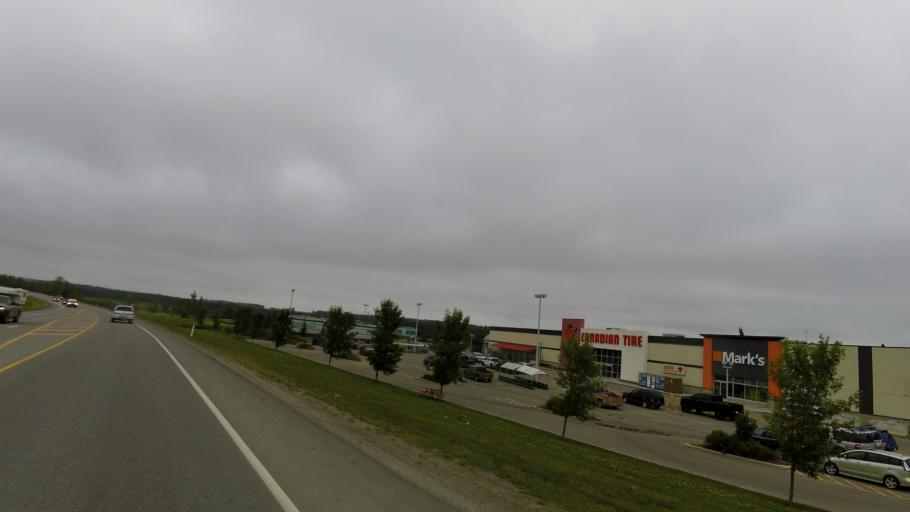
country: CA
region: Alberta
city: Rocky Mountain House
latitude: 52.3815
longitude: -114.9150
